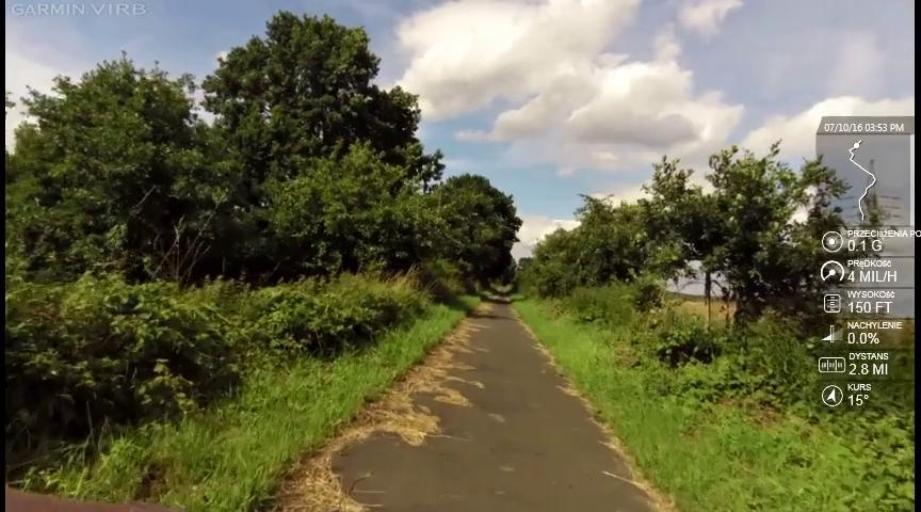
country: PL
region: West Pomeranian Voivodeship
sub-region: Powiat gryfinski
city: Banie
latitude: 53.1462
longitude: 14.6224
